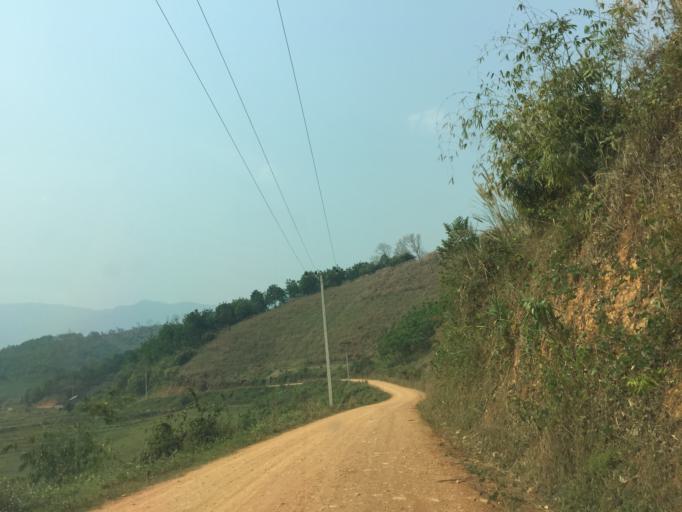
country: TH
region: Phayao
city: Phu Sang
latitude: 19.5768
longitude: 100.5269
